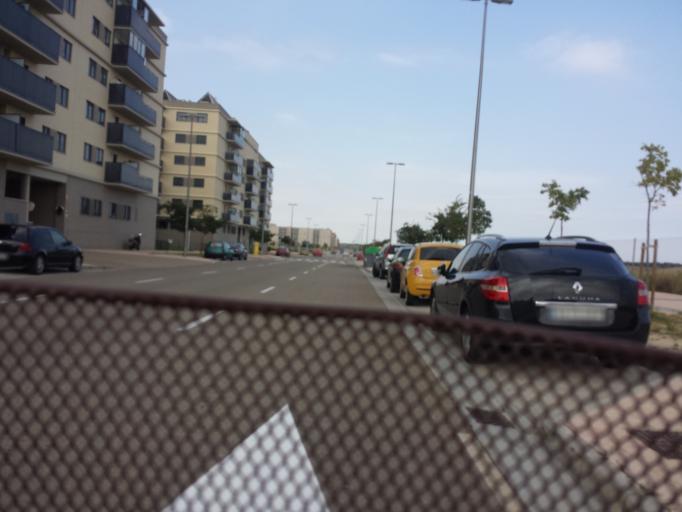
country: ES
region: Aragon
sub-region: Provincia de Zaragoza
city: Montecanal
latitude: 41.6239
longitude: -0.9518
